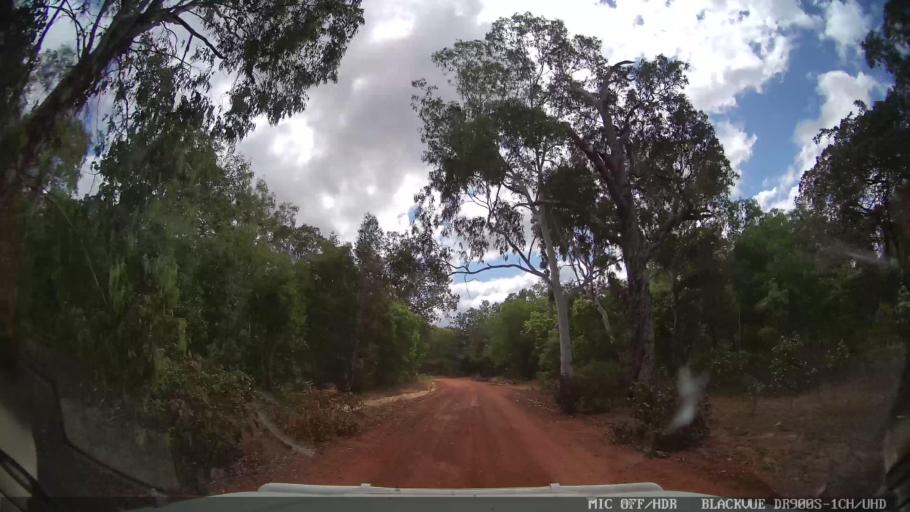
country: AU
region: Queensland
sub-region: Cook
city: Cooktown
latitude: -15.3034
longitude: 144.6148
